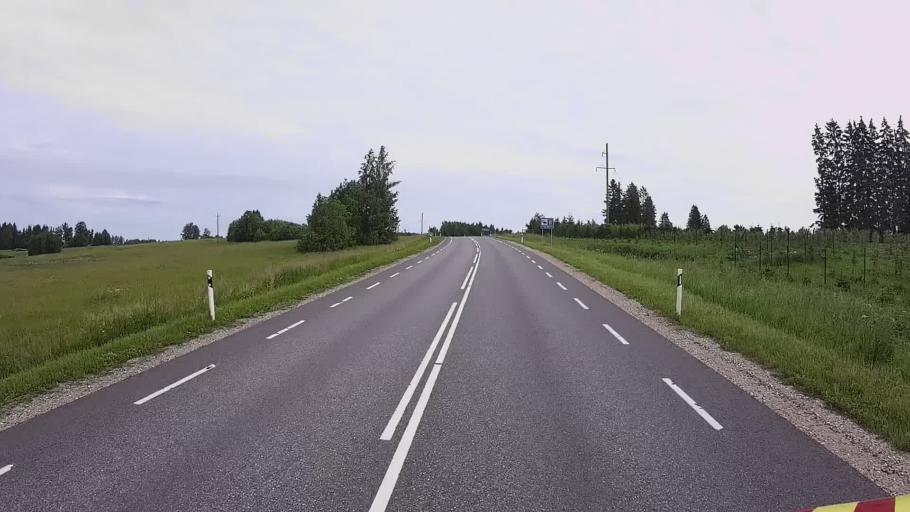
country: EE
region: Viljandimaa
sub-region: Karksi vald
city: Karksi-Nuia
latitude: 58.1495
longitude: 25.5952
